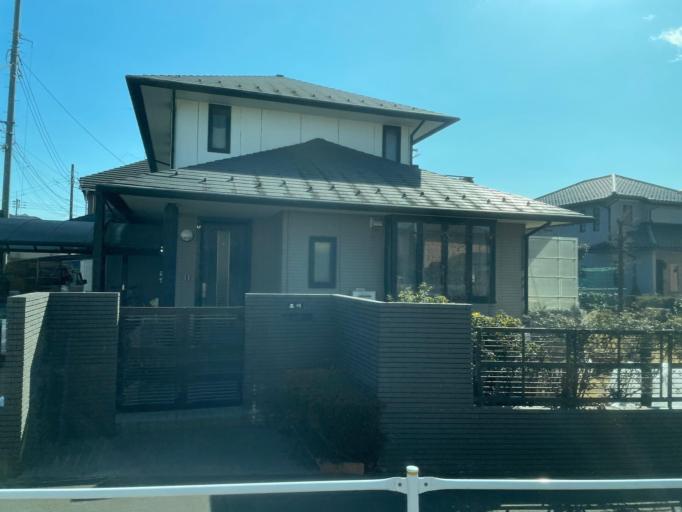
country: JP
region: Tokyo
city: Fussa
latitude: 35.7548
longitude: 139.3631
